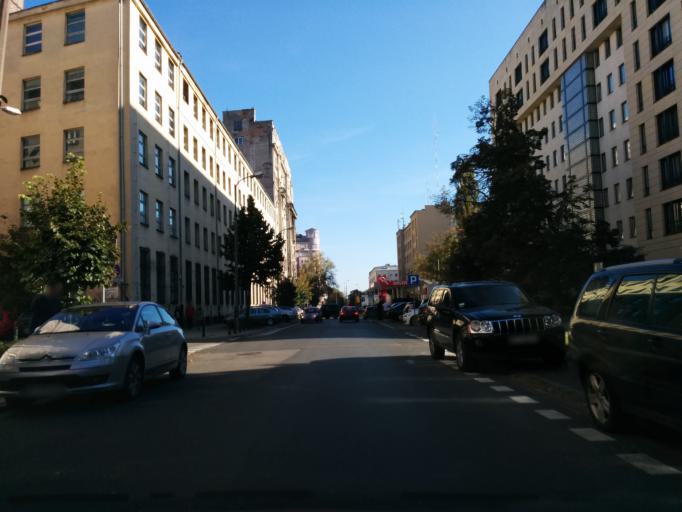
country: PL
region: Masovian Voivodeship
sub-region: Warszawa
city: Srodmiescie
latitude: 52.2151
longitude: 21.0194
